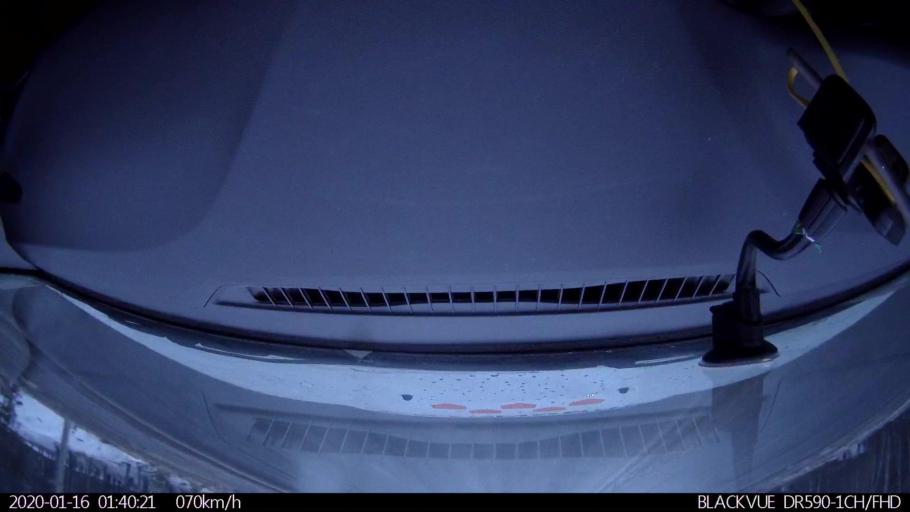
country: RU
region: Nizjnij Novgorod
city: Gorbatovka
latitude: 56.3276
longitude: 43.7806
